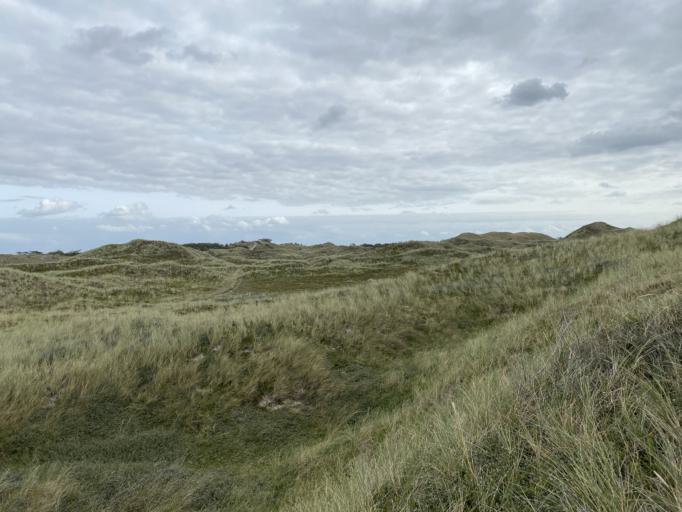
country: DK
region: Central Jutland
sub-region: Holstebro Kommune
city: Ulfborg
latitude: 56.3031
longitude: 8.1253
